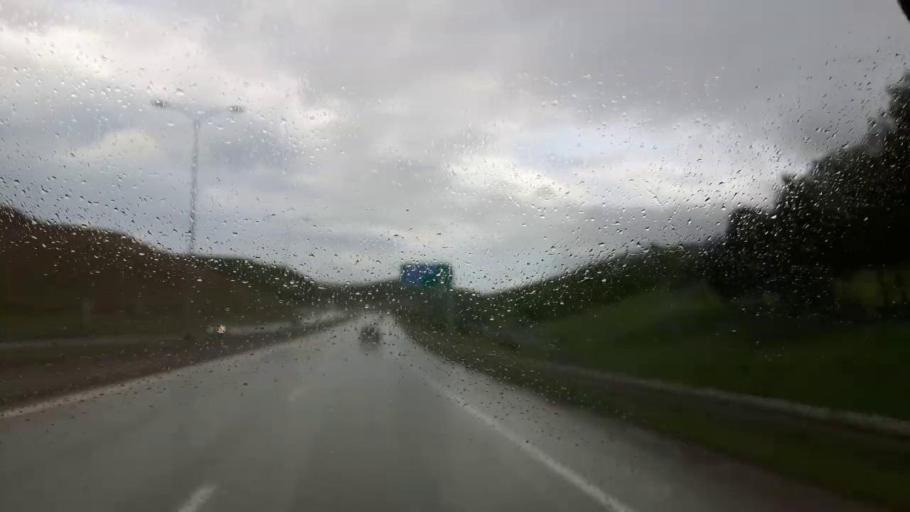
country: GE
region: Shida Kartli
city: Kaspi
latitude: 41.9982
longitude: 44.3977
